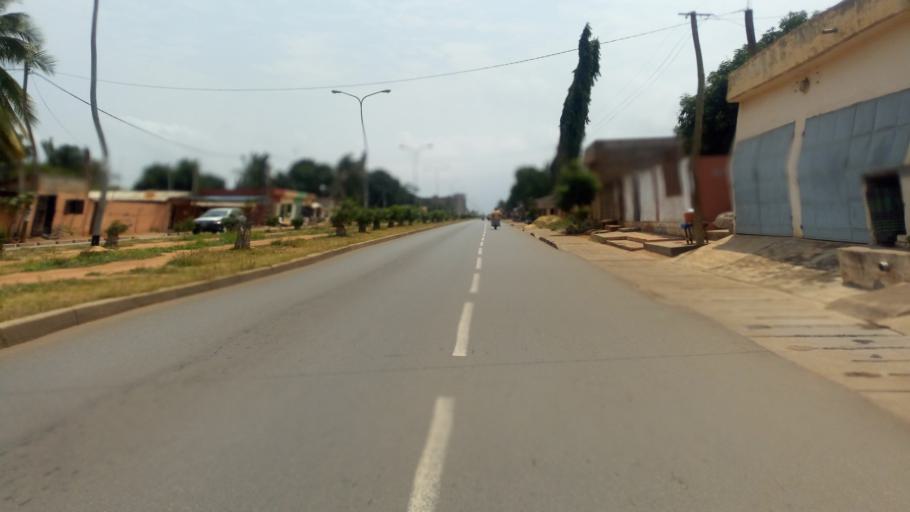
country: TG
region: Maritime
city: Lome
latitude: 6.1908
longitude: 1.2495
